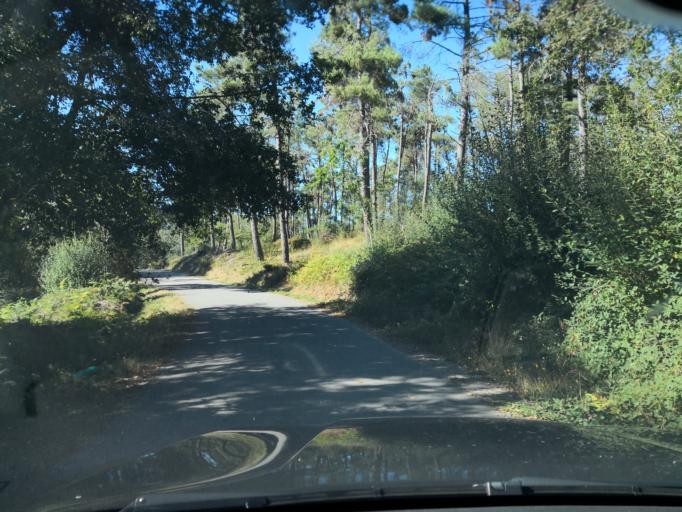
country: PT
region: Vila Real
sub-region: Santa Marta de Penaguiao
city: Santa Marta de Penaguiao
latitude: 41.2935
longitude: -7.8652
